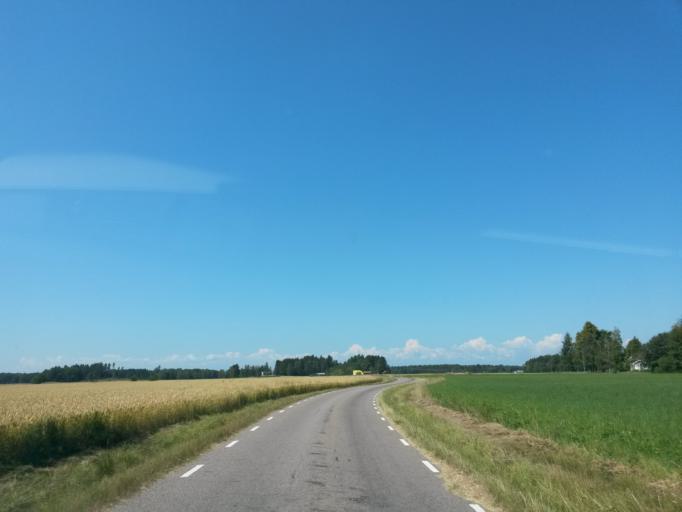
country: SE
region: Vaestra Goetaland
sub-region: Grastorps Kommun
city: Graestorp
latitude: 58.3774
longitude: 12.7868
